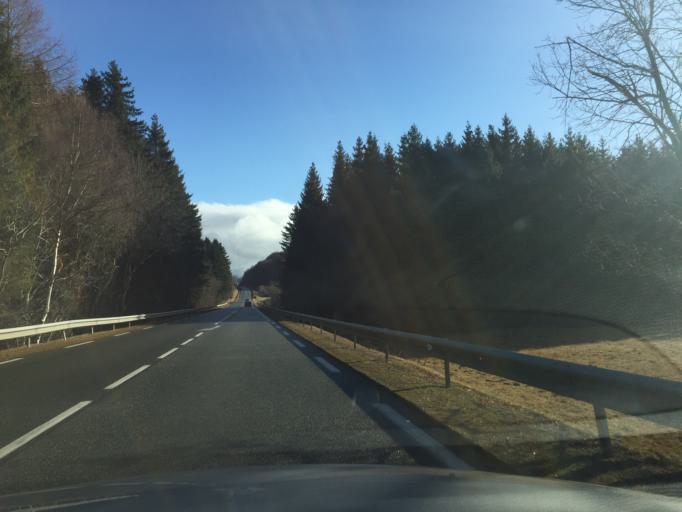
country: FR
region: Auvergne
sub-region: Departement du Puy-de-Dome
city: Orcines
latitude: 45.8088
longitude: 2.9692
